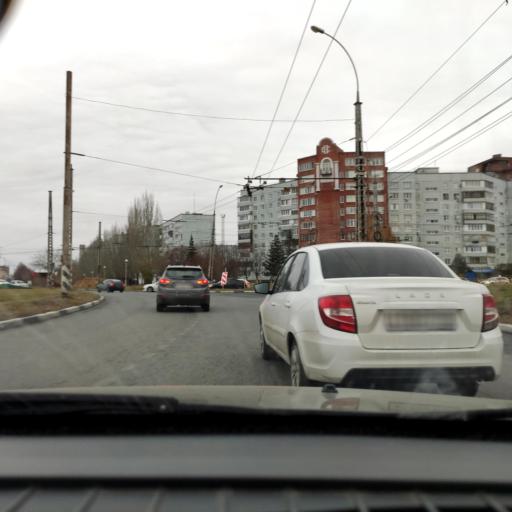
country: RU
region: Samara
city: Tol'yatti
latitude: 53.5252
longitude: 49.3273
